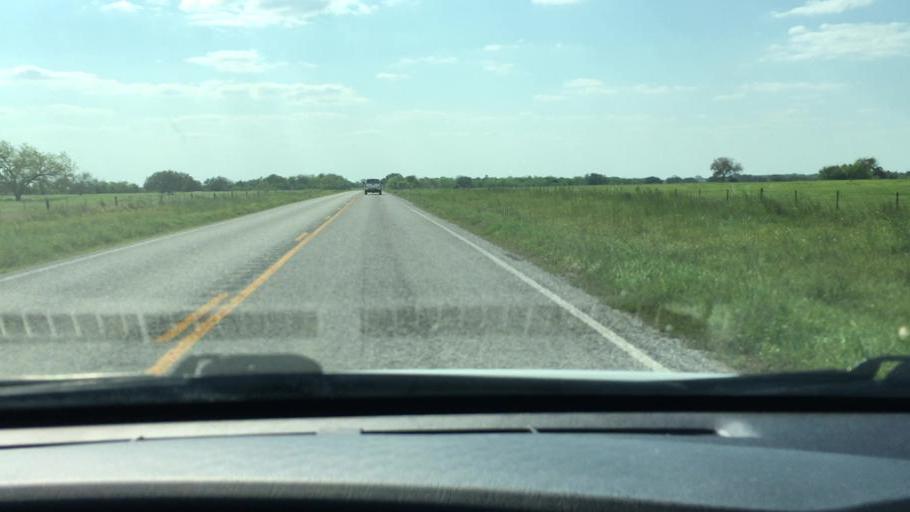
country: US
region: Texas
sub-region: DeWitt County
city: Yorktown
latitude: 28.9188
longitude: -97.3366
